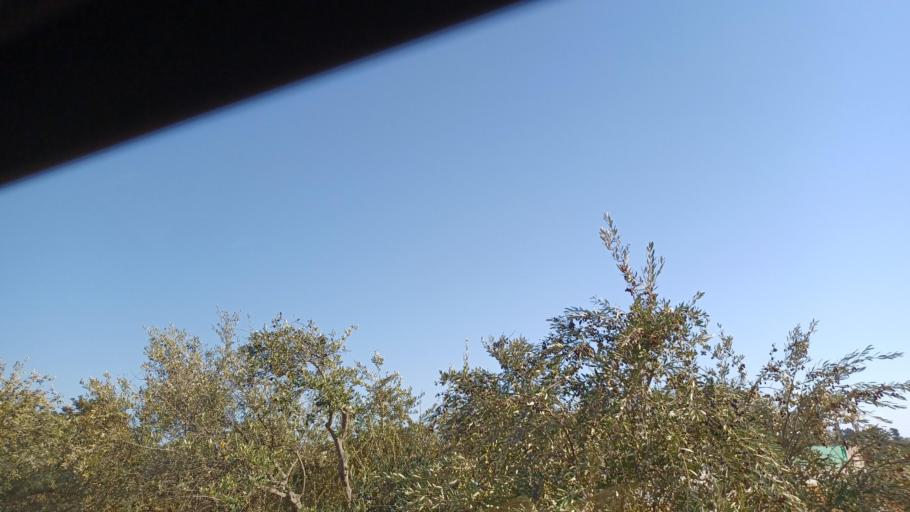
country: CY
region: Larnaka
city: Kolossi
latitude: 34.6689
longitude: 32.9499
